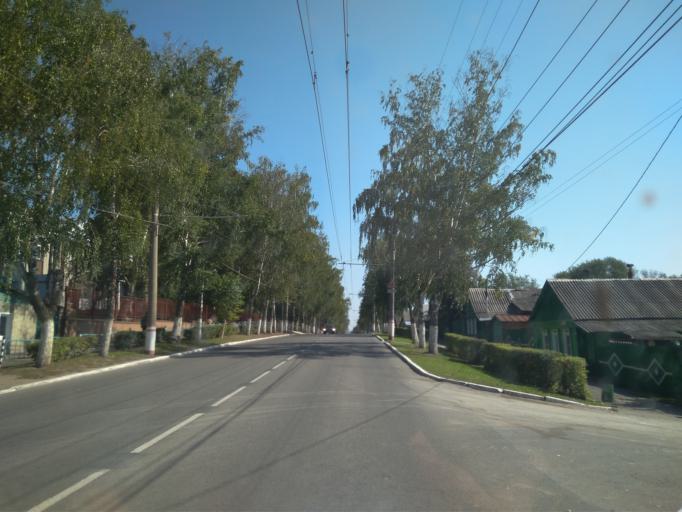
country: RU
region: Mordoviya
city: Saransk
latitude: 54.1851
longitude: 45.1630
